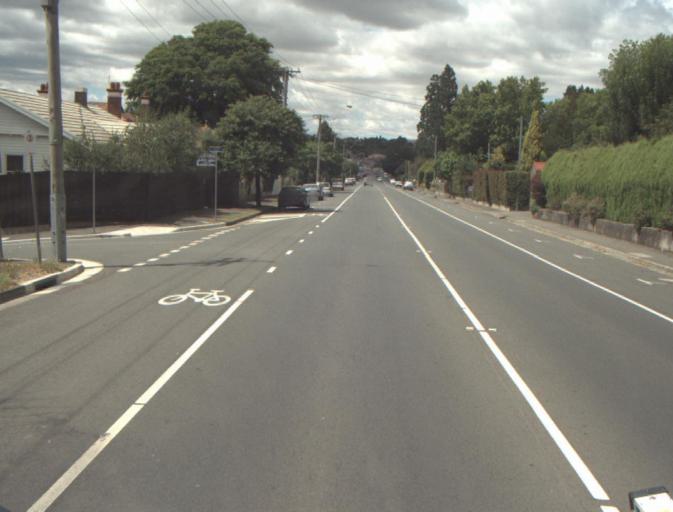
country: AU
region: Tasmania
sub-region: Launceston
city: East Launceston
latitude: -41.4379
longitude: 147.1582
